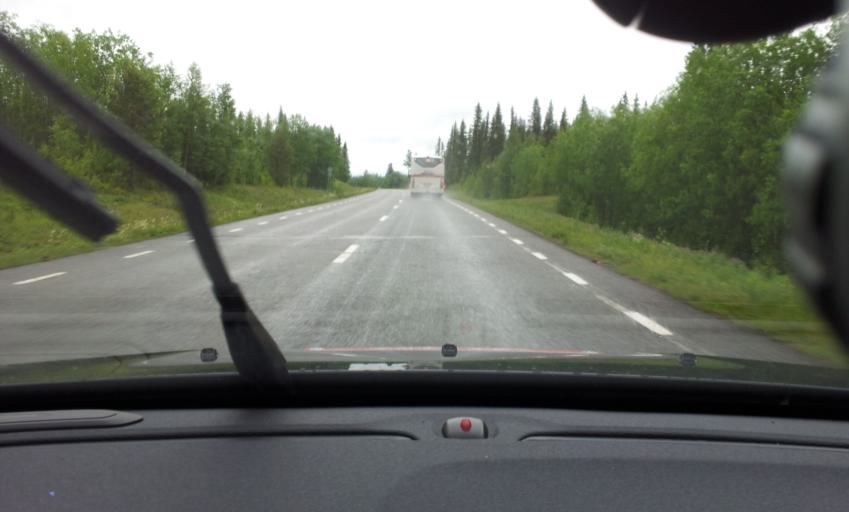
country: SE
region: Jaemtland
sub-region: Krokoms Kommun
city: Krokom
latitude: 63.5717
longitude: 14.6267
